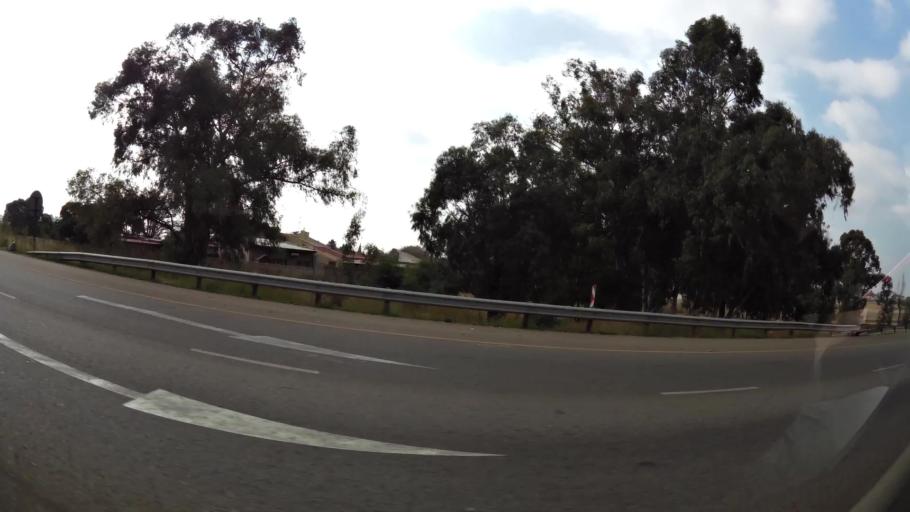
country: ZA
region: Gauteng
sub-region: City of Johannesburg Metropolitan Municipality
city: Modderfontein
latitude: -26.1136
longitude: 28.2558
